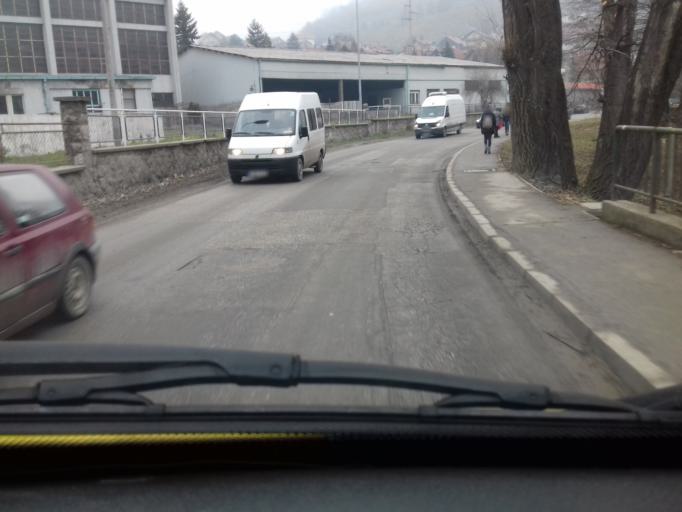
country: BA
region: Federation of Bosnia and Herzegovina
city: Zenica
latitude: 44.2094
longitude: 17.9280
